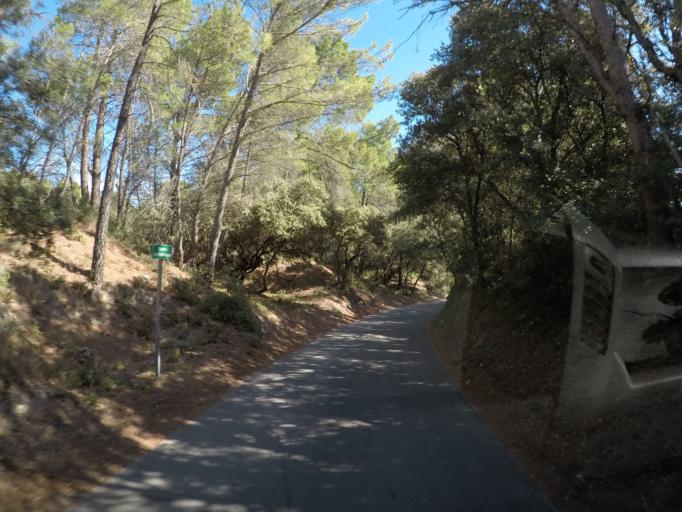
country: FR
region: Rhone-Alpes
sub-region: Departement de la Drome
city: Suze-la-Rousse
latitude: 44.2892
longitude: 4.8036
